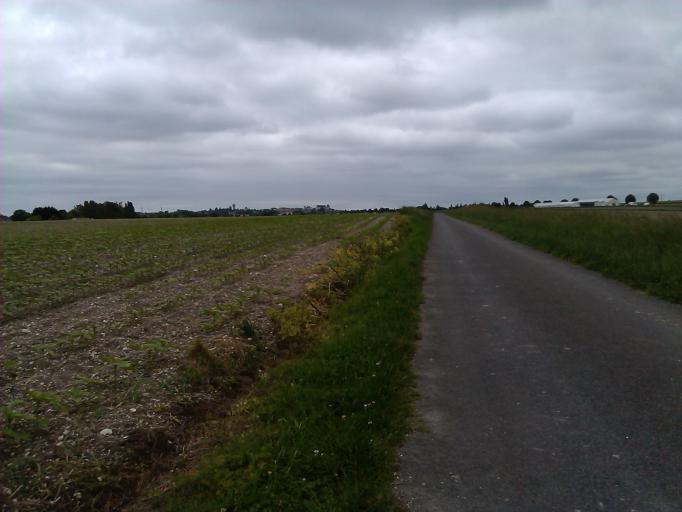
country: FR
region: Poitou-Charentes
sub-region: Departement de la Charente
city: Barbezieux-Saint-Hilaire
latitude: 45.4911
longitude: -0.1374
